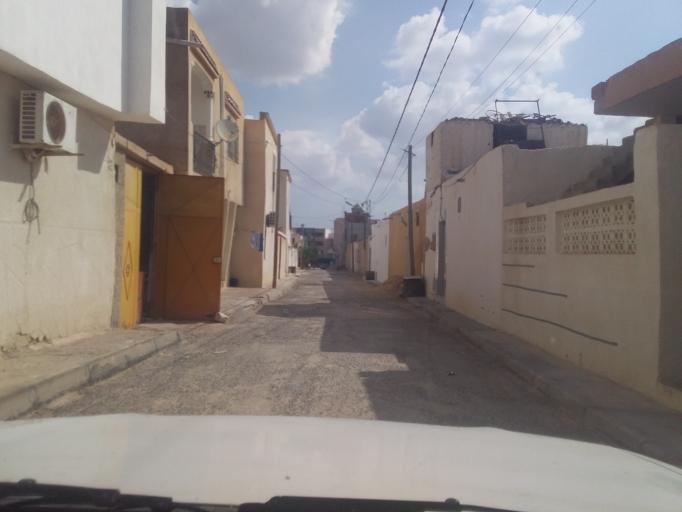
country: TN
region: Qabis
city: Gabes
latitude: 33.6236
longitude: 10.2800
